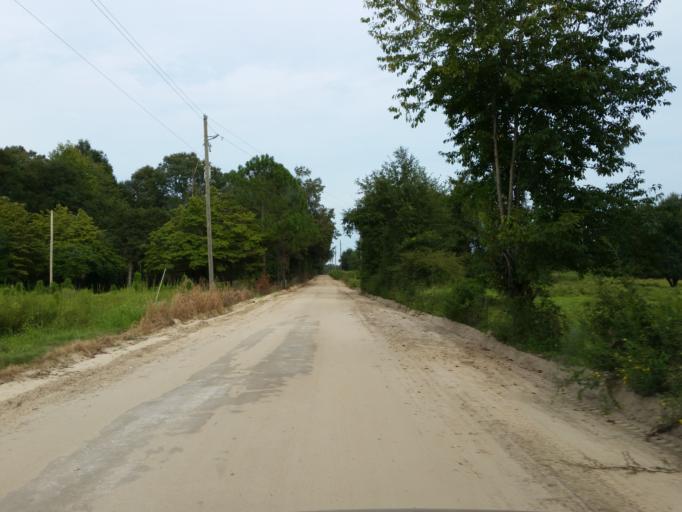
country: US
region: Florida
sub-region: Madison County
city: Madison
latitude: 30.5374
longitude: -83.2017
